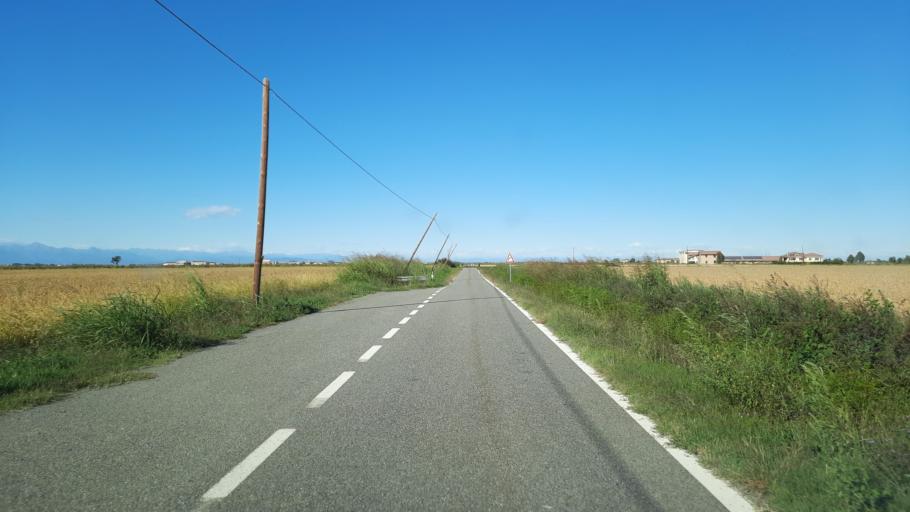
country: IT
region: Piedmont
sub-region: Provincia di Vercelli
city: Ronsecco
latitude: 45.2613
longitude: 8.2846
